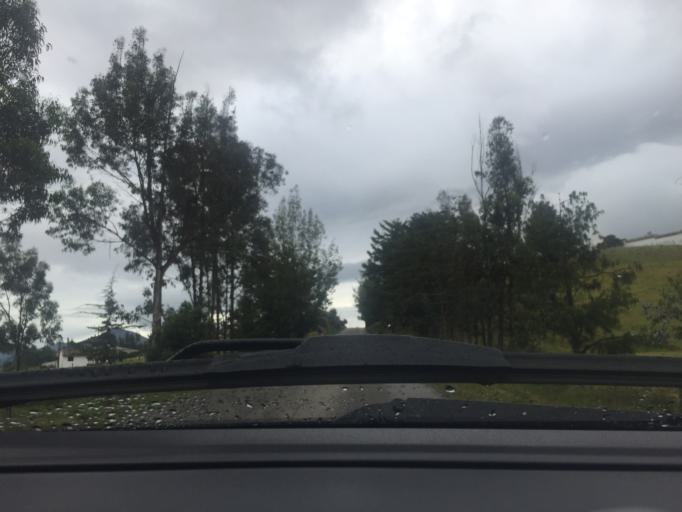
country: CO
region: Cundinamarca
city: Guasca
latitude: 4.8701
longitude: -73.8826
